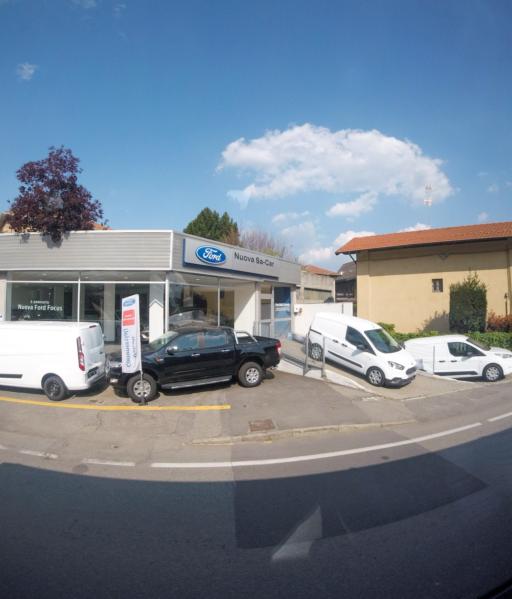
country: IT
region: Piedmont
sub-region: Provincia di Novara
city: Arona
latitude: 45.7538
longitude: 8.5587
